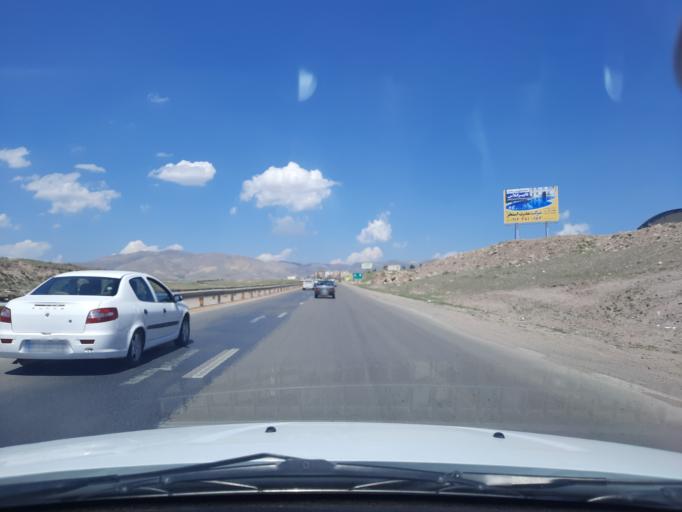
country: IR
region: Qazvin
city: Alvand
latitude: 36.2830
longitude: 50.1298
